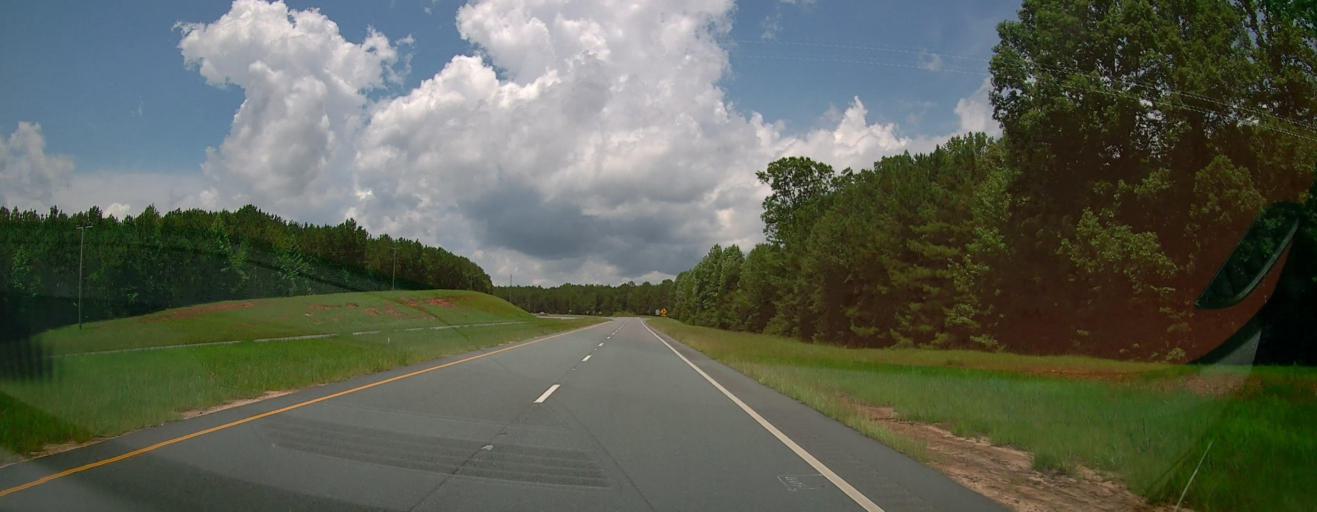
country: US
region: Georgia
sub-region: Upson County
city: Thomaston
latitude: 32.7854
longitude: -84.2472
